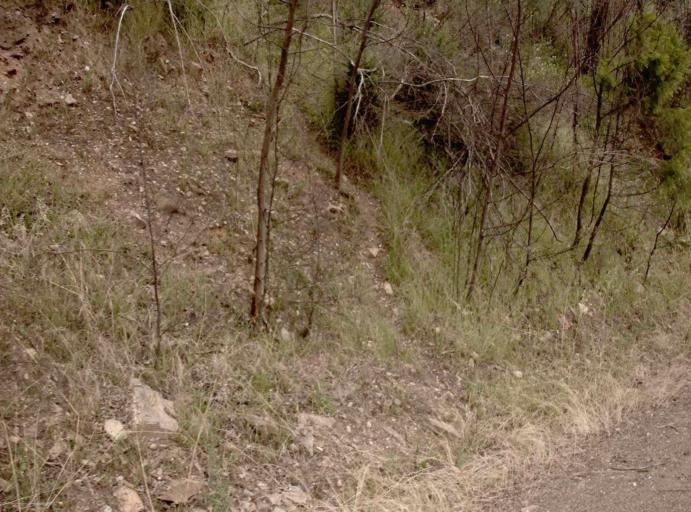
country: AU
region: Victoria
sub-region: Wellington
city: Heyfield
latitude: -37.7816
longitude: 146.6665
